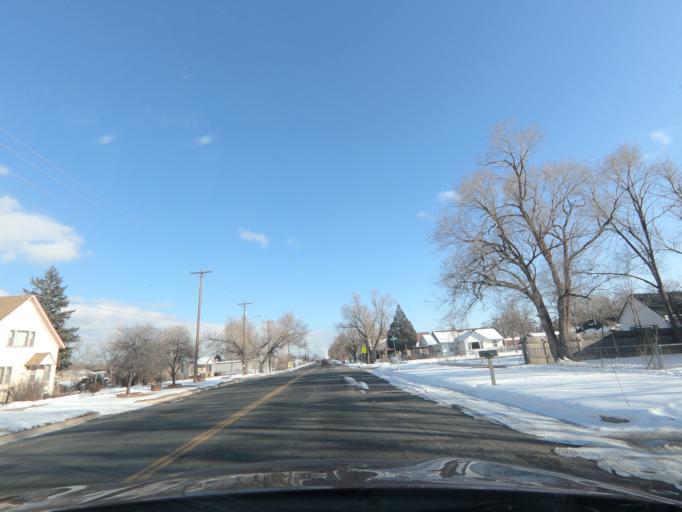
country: US
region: Colorado
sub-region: El Paso County
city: Colorado Springs
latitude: 38.8422
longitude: -104.8659
